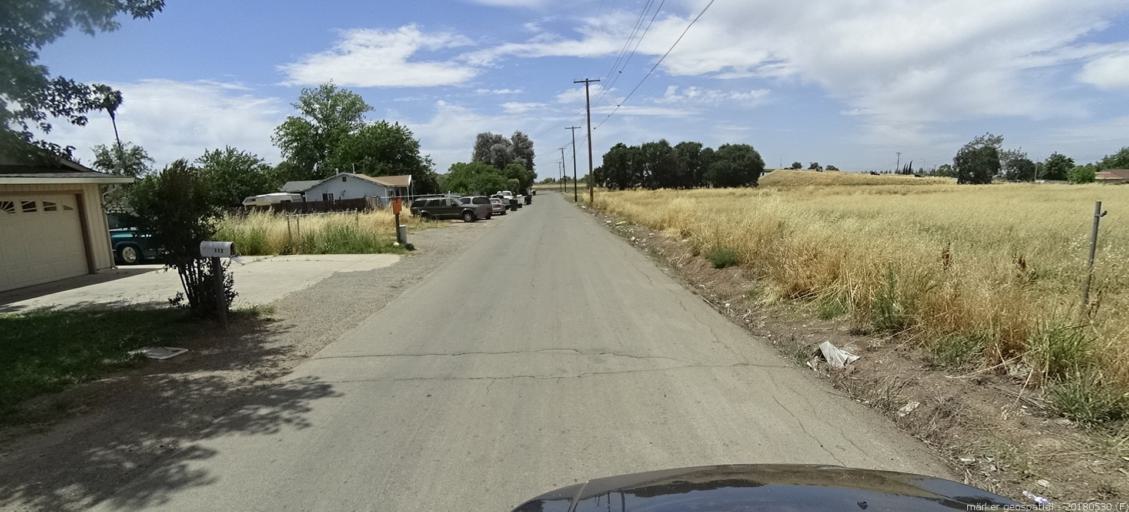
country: US
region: California
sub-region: Sacramento County
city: Sacramento
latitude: 38.6287
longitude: -121.4651
